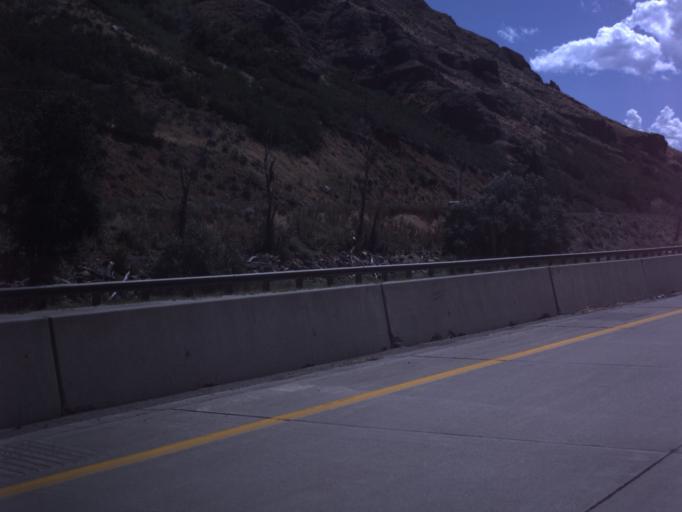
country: US
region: Utah
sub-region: Morgan County
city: Morgan
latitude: 41.0542
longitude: -111.5305
